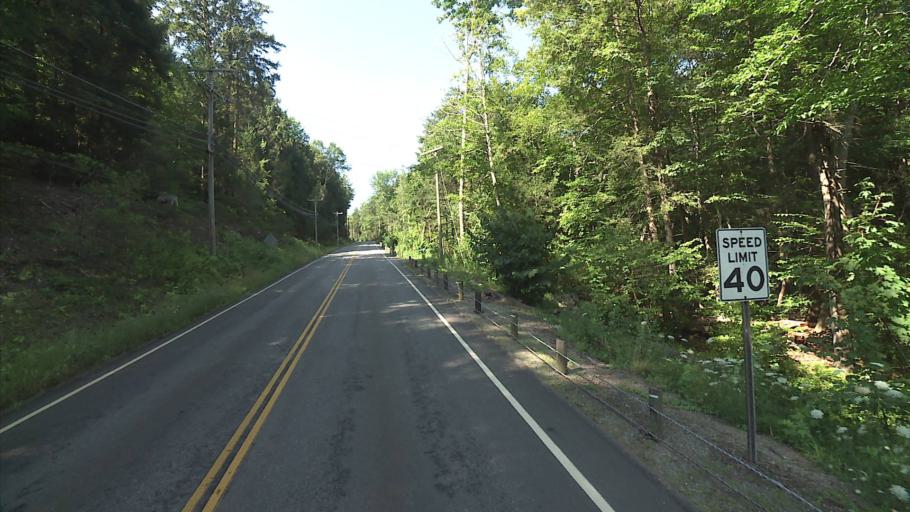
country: US
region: Connecticut
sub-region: Litchfield County
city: Winsted
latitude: 41.9585
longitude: -73.0251
